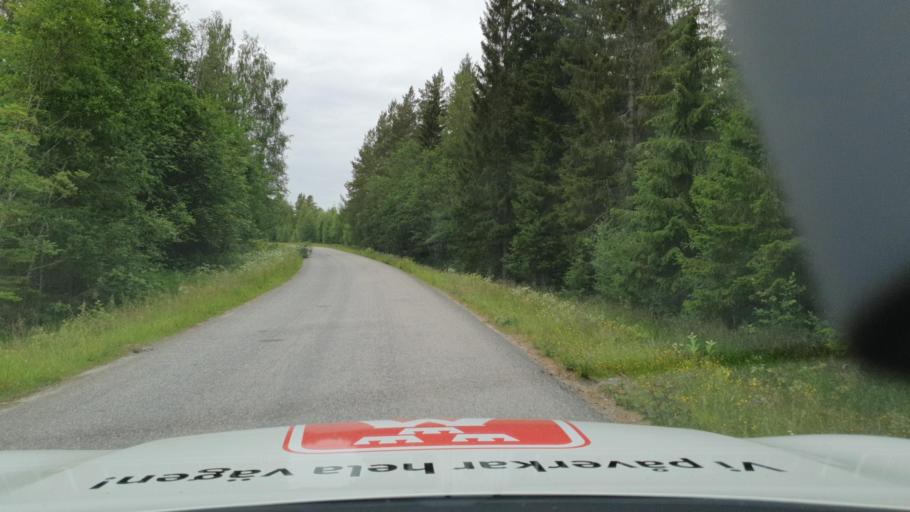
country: SE
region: Vaesterbotten
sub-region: Nordmalings Kommun
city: Nordmaling
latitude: 63.5311
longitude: 19.4320
